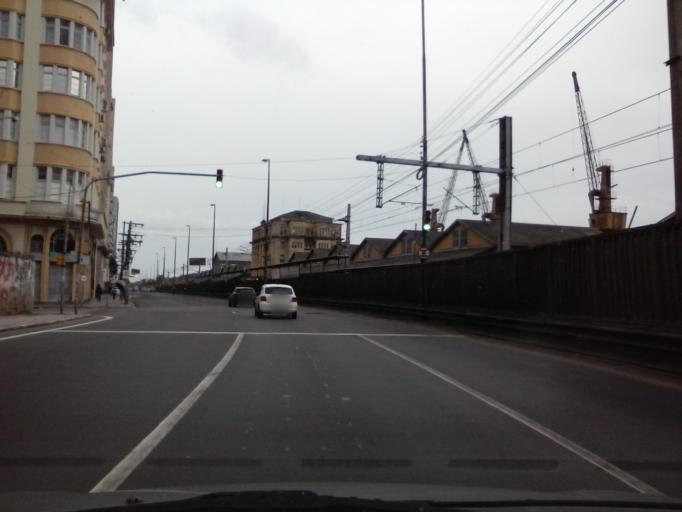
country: BR
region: Rio Grande do Sul
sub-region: Porto Alegre
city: Porto Alegre
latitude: -30.0266
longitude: -51.2292
